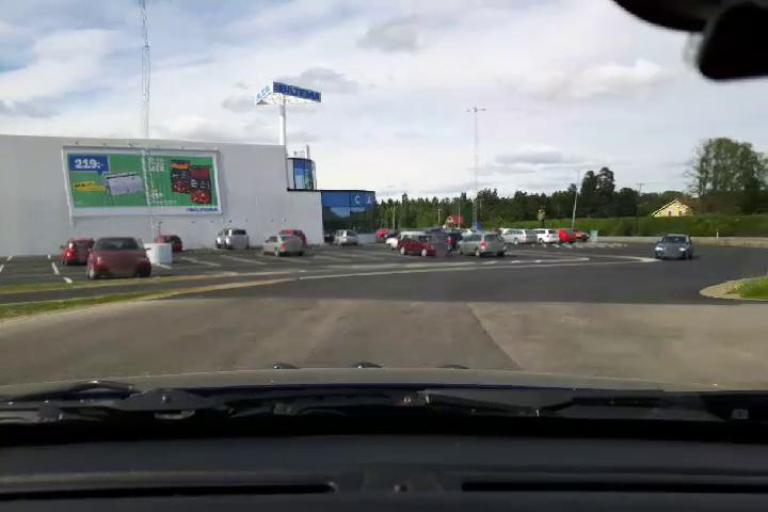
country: SE
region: Gaevleborg
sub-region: Bollnas Kommun
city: Bollnas
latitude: 61.3674
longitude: 16.3932
